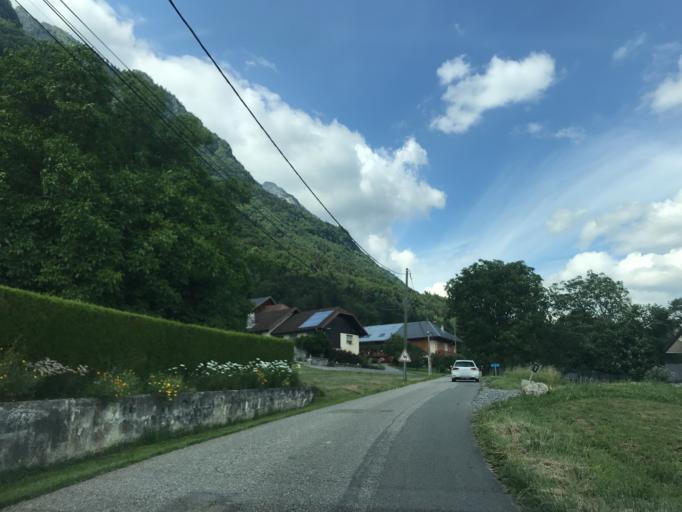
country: FR
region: Rhone-Alpes
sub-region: Departement de la Savoie
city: Mercury
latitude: 45.6792
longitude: 6.3406
